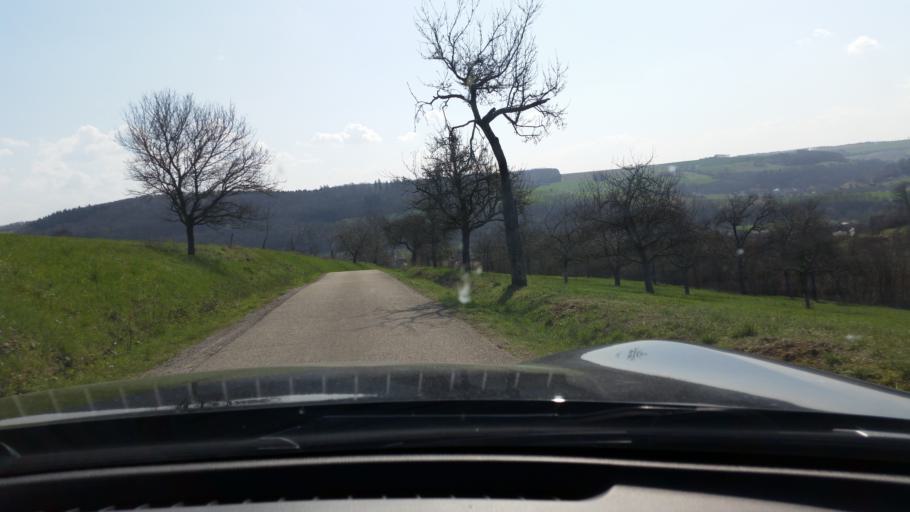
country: DE
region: Baden-Wuerttemberg
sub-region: Regierungsbezirk Stuttgart
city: Krautheim
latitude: 49.3753
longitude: 9.6091
